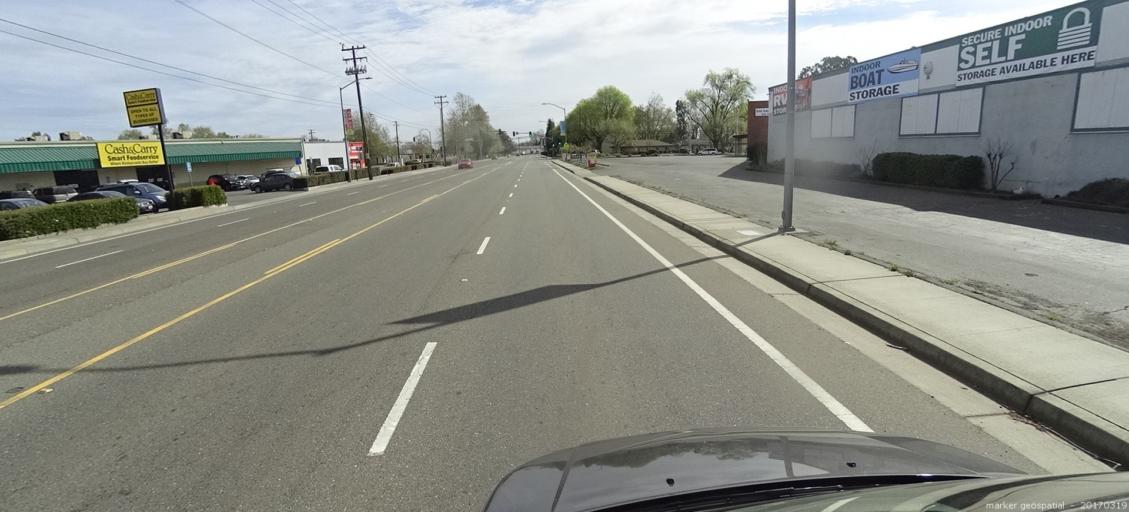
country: US
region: California
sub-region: Sacramento County
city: Sacramento
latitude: 38.5951
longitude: -121.4857
